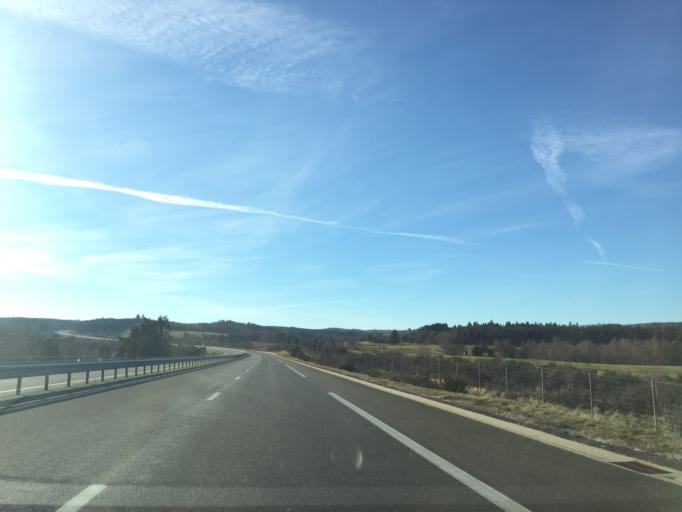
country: FR
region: Auvergne
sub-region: Departement du Puy-de-Dome
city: Gelles
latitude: 45.7745
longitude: 2.7371
